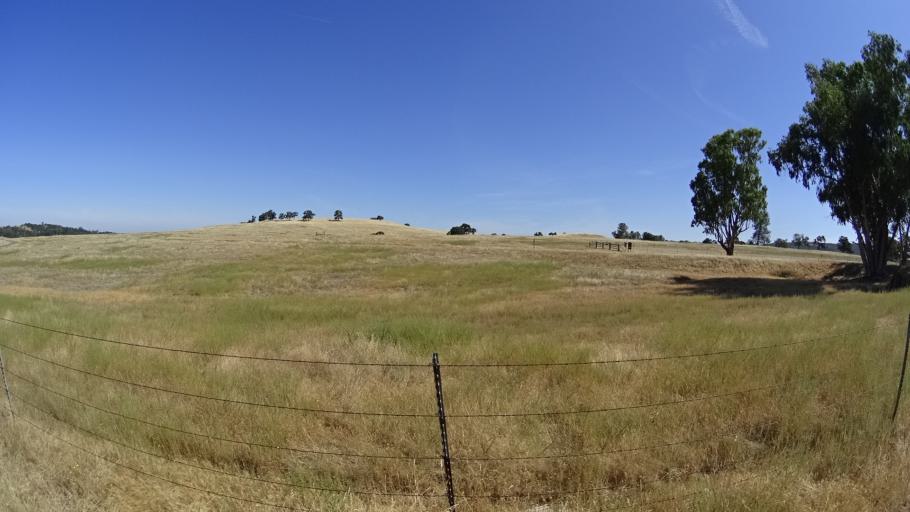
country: US
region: California
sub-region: Calaveras County
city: Valley Springs
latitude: 38.2296
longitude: -120.8321
